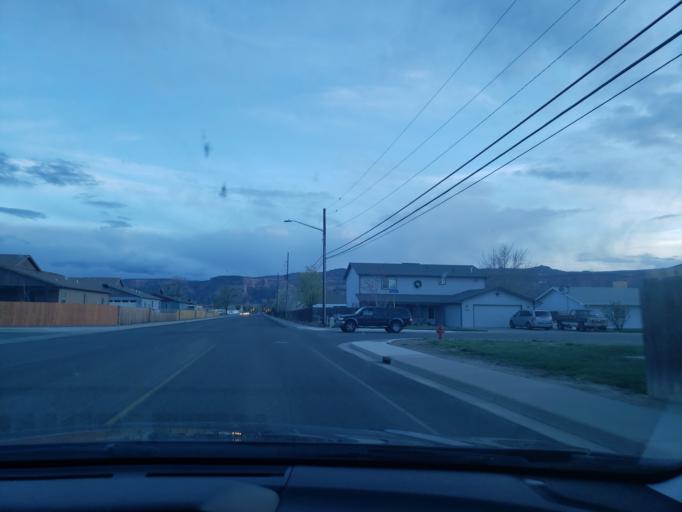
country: US
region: Colorado
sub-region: Mesa County
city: Fruita
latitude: 39.1528
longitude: -108.7198
